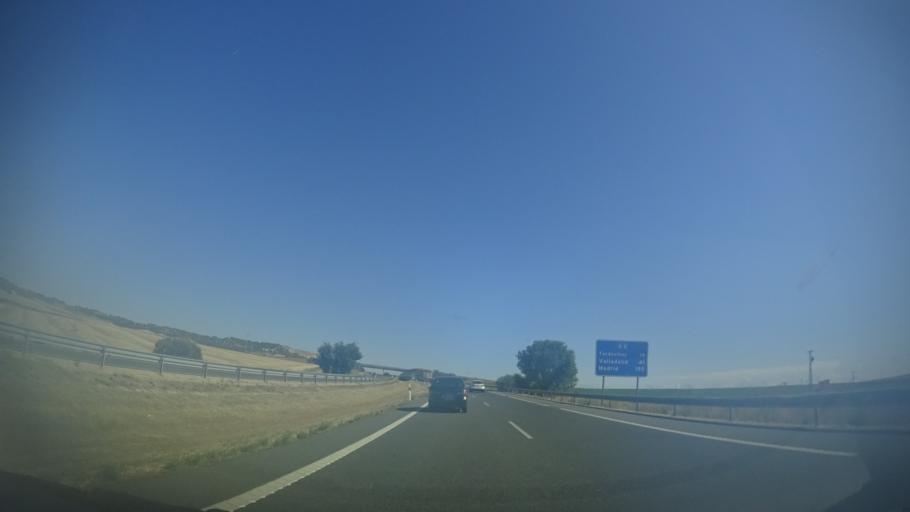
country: ES
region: Castille and Leon
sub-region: Provincia de Valladolid
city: Vega de Valdetronco
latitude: 41.5847
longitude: -5.1105
